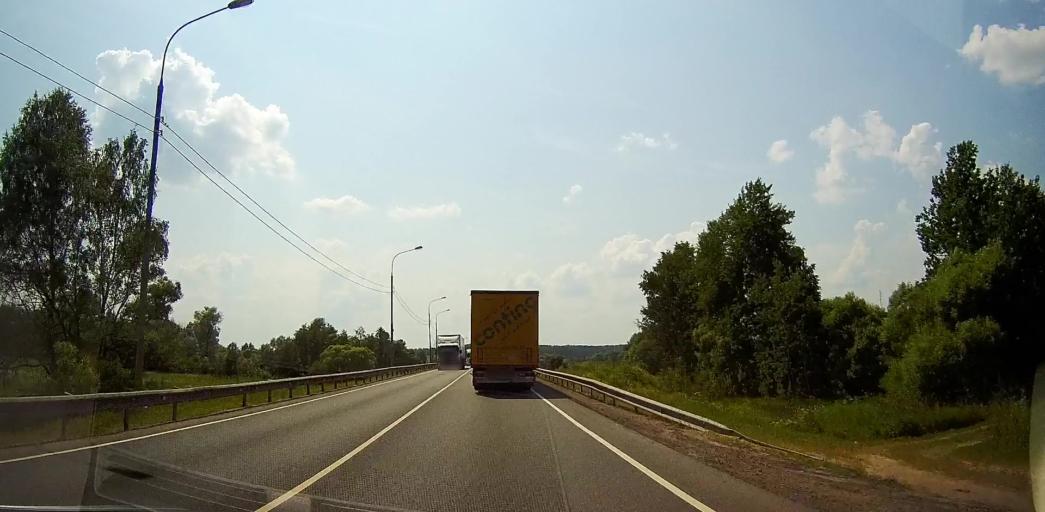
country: RU
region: Moskovskaya
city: Meshcherino
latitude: 55.1911
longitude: 38.3619
